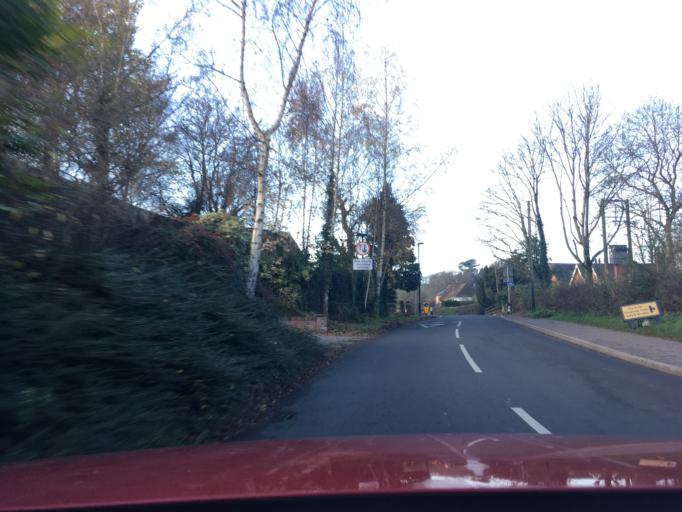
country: GB
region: England
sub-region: Staffordshire
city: Barton under Needwood
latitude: 52.7912
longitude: -1.6963
